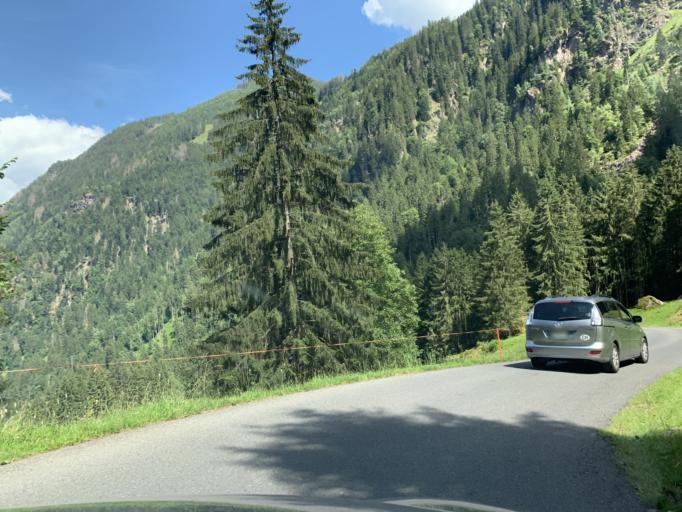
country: CH
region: Saint Gallen
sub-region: Wahlkreis Sarganserland
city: Quarten
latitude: 47.0847
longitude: 9.1997
